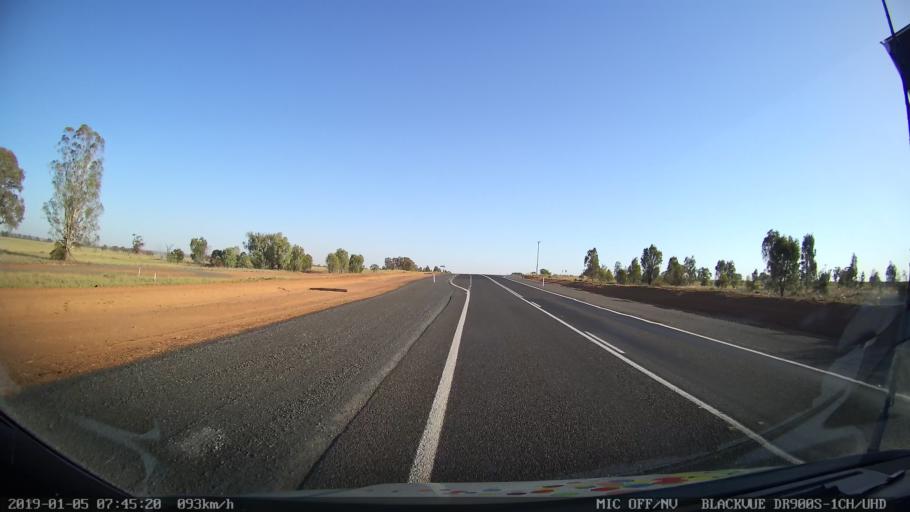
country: AU
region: New South Wales
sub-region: Gilgandra
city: Gilgandra
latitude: -31.8596
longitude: 148.6421
